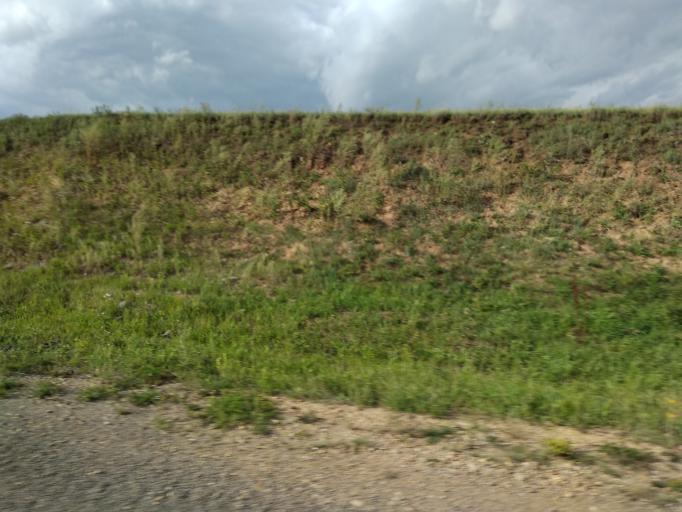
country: RU
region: Irkutsk
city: Bayanday
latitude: 52.9649
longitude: 105.3356
